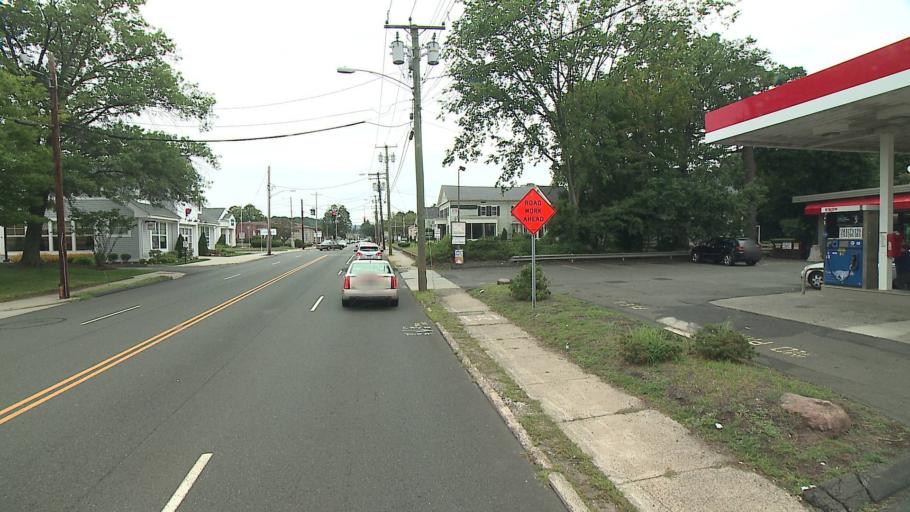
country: US
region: Connecticut
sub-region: New Haven County
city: Hamden
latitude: 41.3802
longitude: -72.9030
